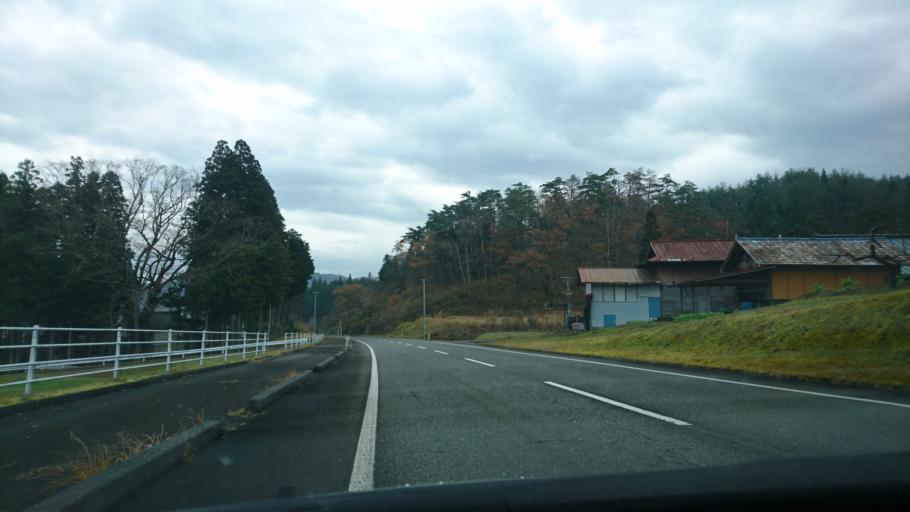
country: JP
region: Iwate
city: Ichinoseki
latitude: 38.8961
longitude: 140.9332
